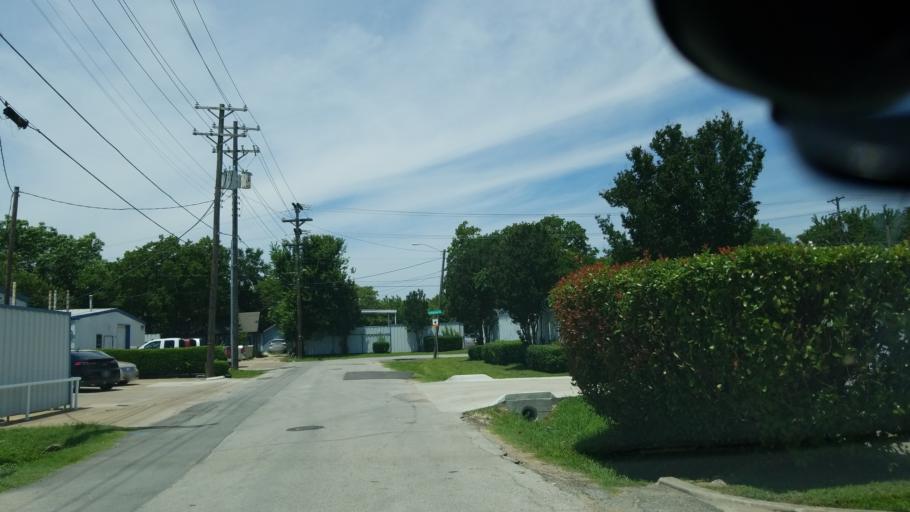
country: US
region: Texas
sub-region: Dallas County
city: Irving
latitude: 32.8159
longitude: -96.9439
